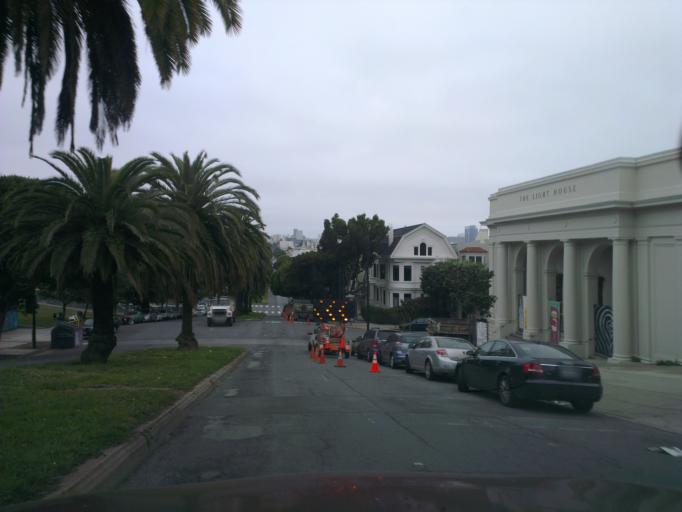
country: US
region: California
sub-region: San Francisco County
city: San Francisco
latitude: 37.7585
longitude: -122.4258
